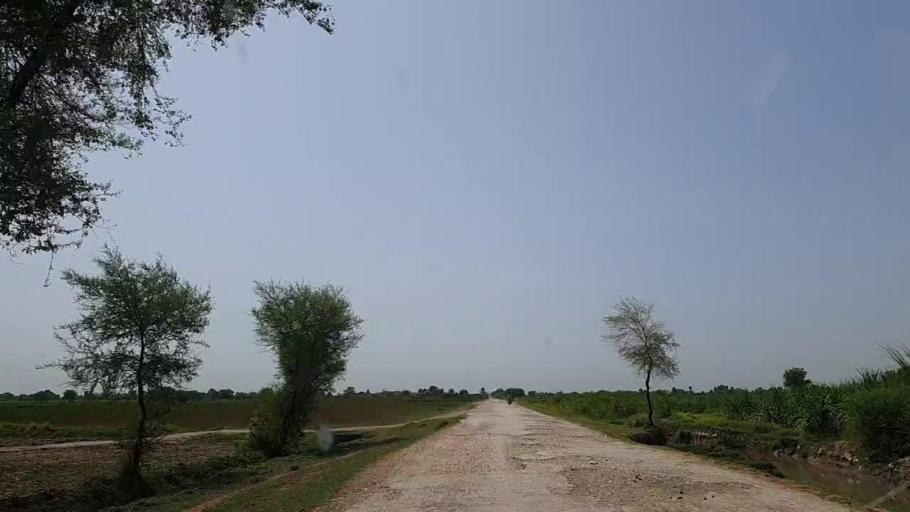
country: PK
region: Sindh
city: Naushahro Firoz
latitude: 26.8541
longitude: 68.0083
